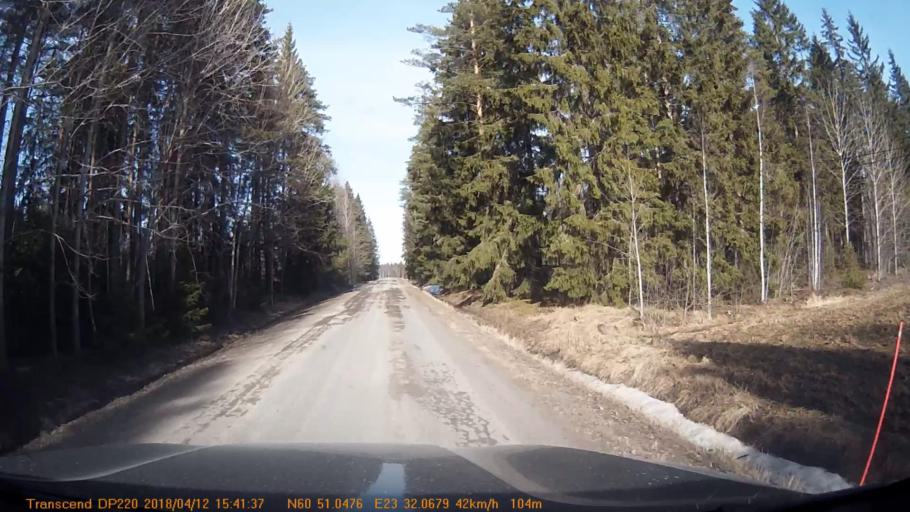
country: FI
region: Haeme
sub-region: Forssa
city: Jokioinen
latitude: 60.8511
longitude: 23.5352
